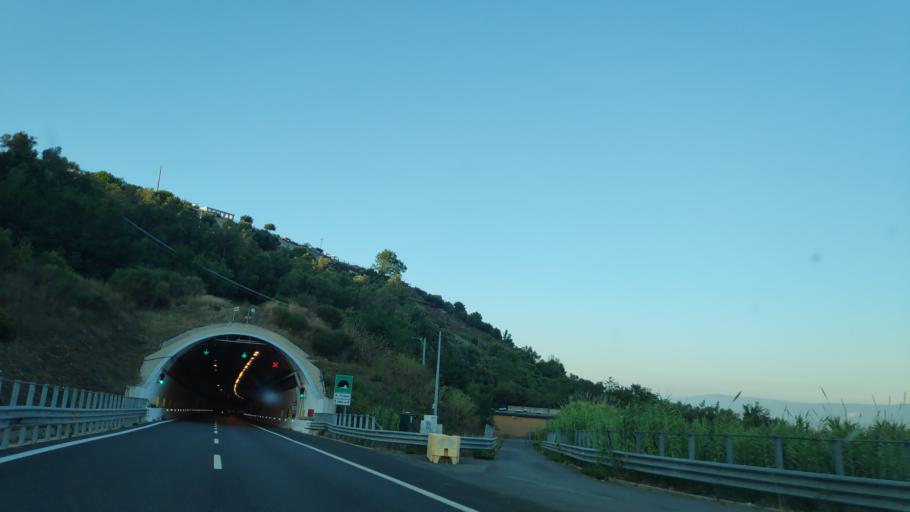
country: IT
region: Calabria
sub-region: Provincia di Reggio Calabria
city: Palmi
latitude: 38.3758
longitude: 15.8708
